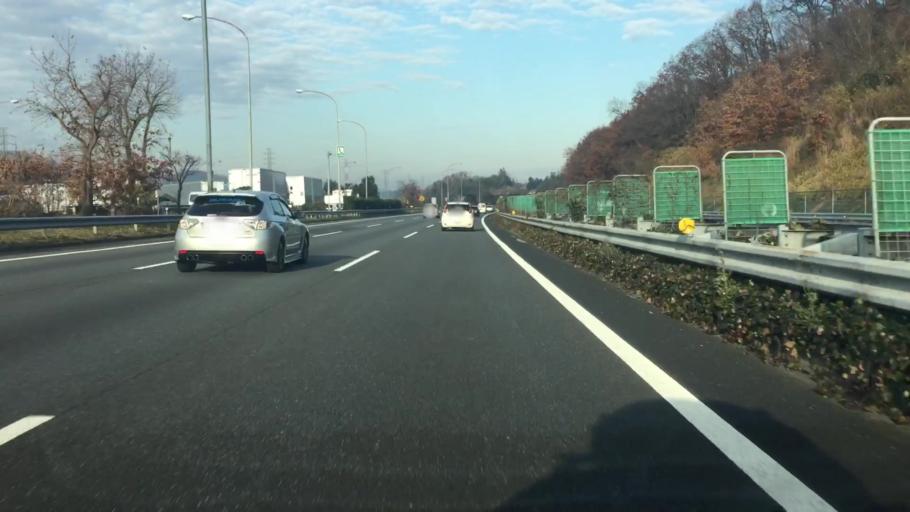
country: JP
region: Saitama
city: Ogawa
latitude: 36.0860
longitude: 139.2921
